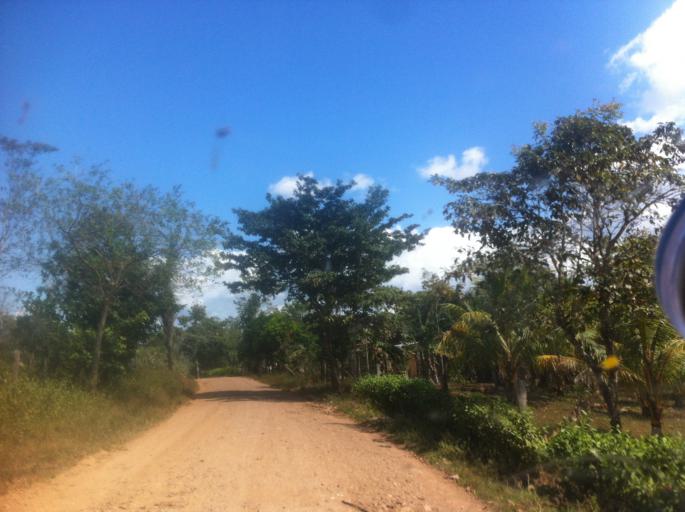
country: CR
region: Alajuela
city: Los Chiles
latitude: 11.2498
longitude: -84.4578
